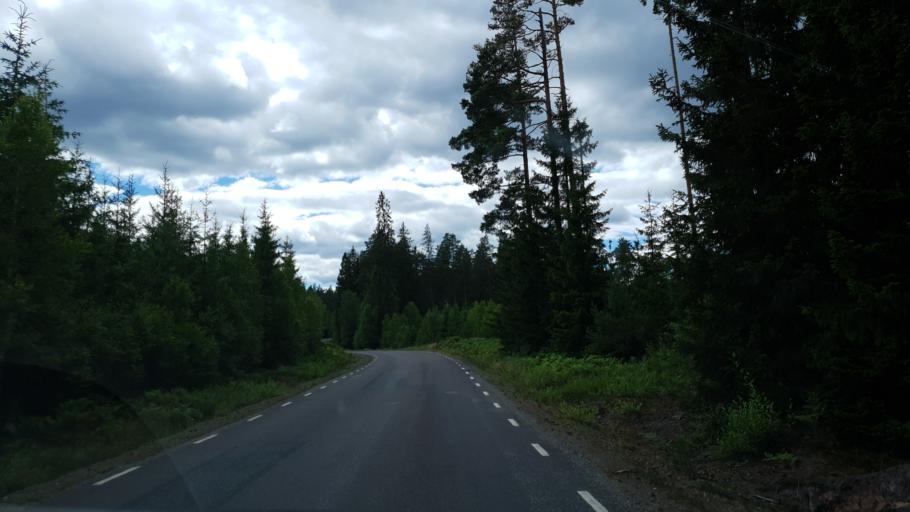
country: SE
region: Kalmar
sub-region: Hultsfreds Kommun
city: Virserum
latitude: 57.0698
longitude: 15.6069
